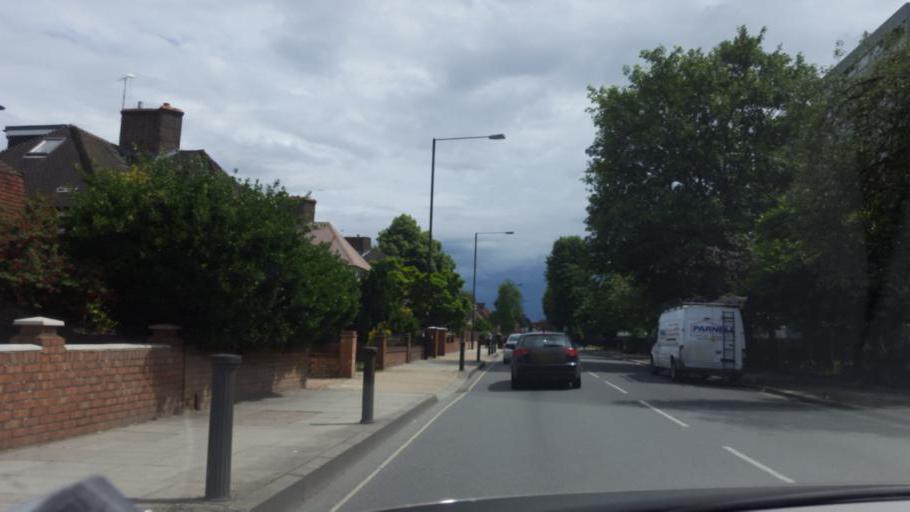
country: GB
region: England
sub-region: Greater London
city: Hammersmith
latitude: 51.5129
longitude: -0.2480
